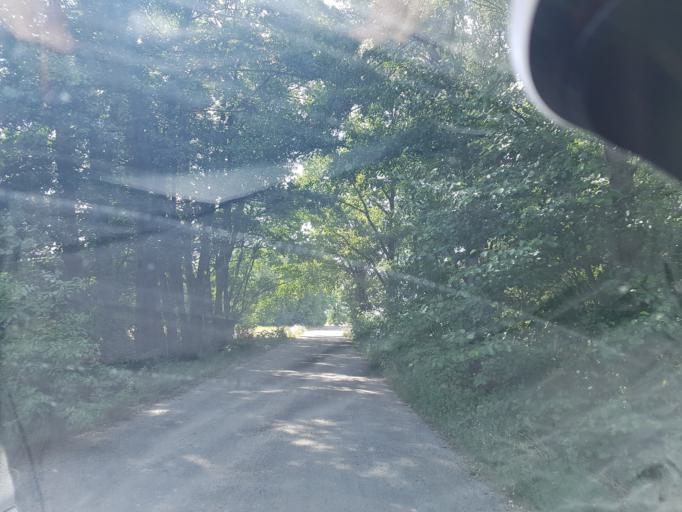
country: DE
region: Brandenburg
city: Cottbus
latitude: 51.7122
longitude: 14.4284
